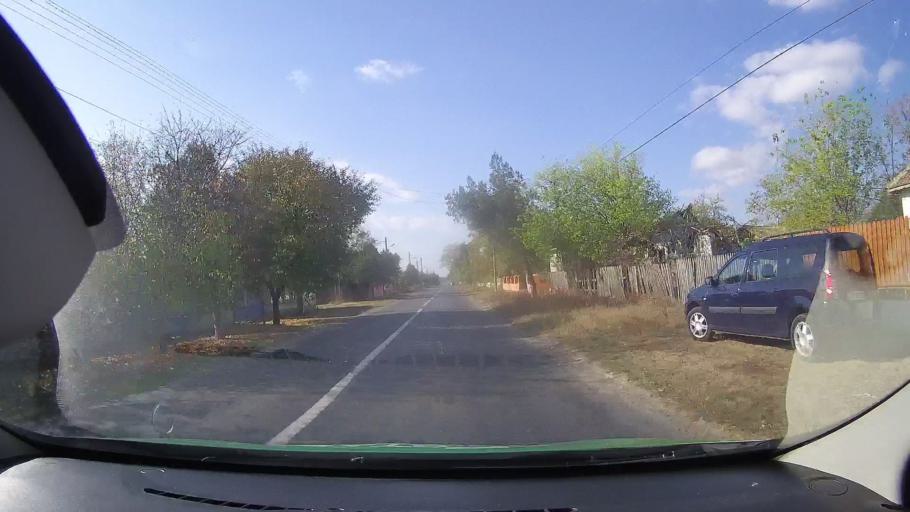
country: RO
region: Constanta
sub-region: Comuna Cogealac
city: Tariverde
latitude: 44.5619
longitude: 28.5905
